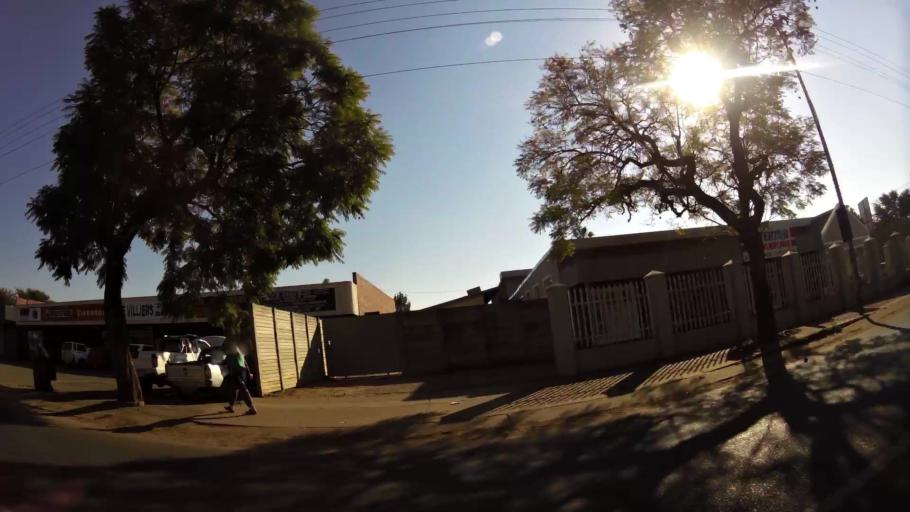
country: ZA
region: Gauteng
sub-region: City of Tshwane Metropolitan Municipality
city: Pretoria
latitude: -25.6654
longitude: 28.1636
